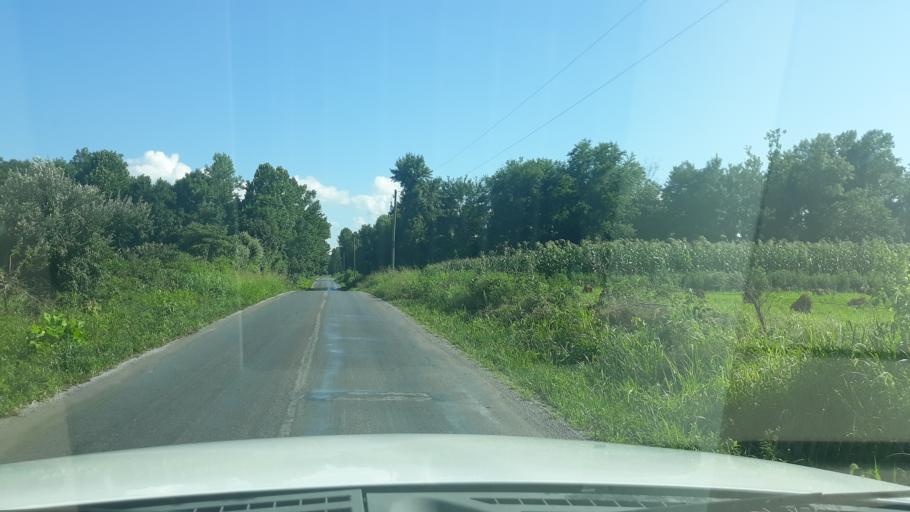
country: US
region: Illinois
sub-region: Saline County
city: Harrisburg
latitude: 37.8630
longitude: -88.5815
